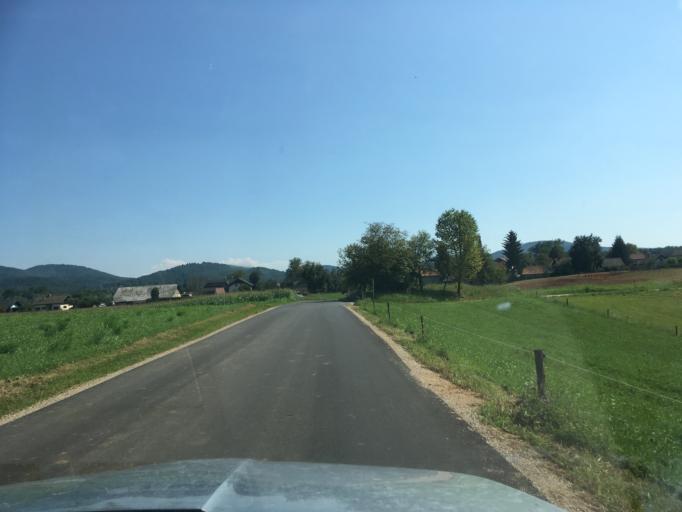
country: SI
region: Metlika
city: Metlika
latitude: 45.5682
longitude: 15.2942
